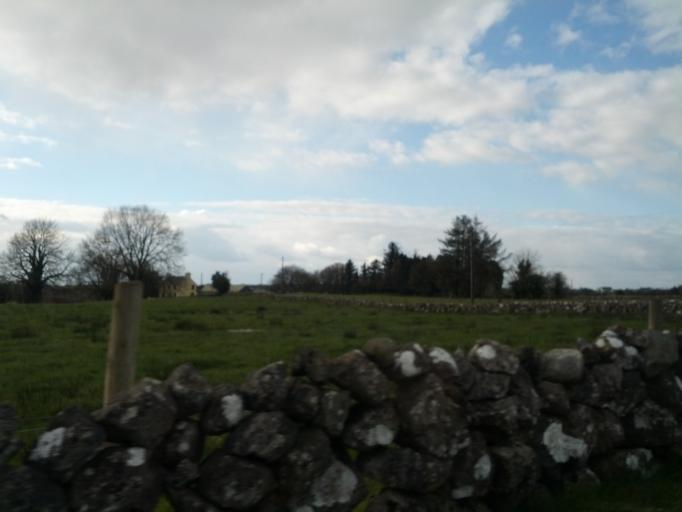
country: IE
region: Connaught
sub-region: County Galway
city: Athenry
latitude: 53.4539
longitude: -8.6430
